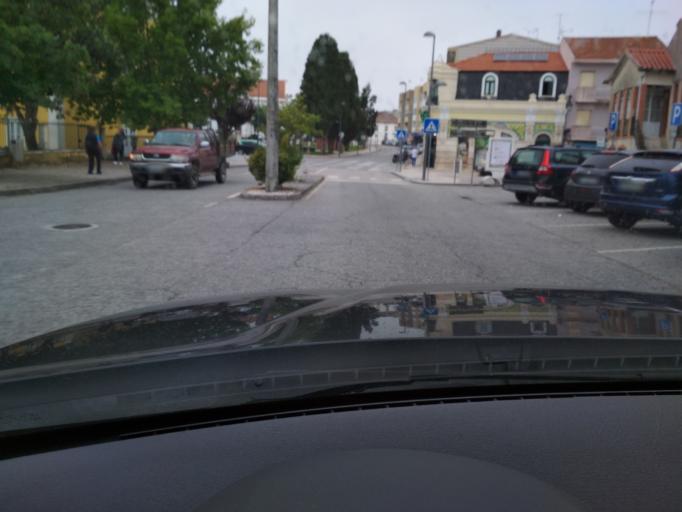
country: PT
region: Aveiro
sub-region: Mealhada
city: Mealhada
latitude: 40.3781
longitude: -8.4510
